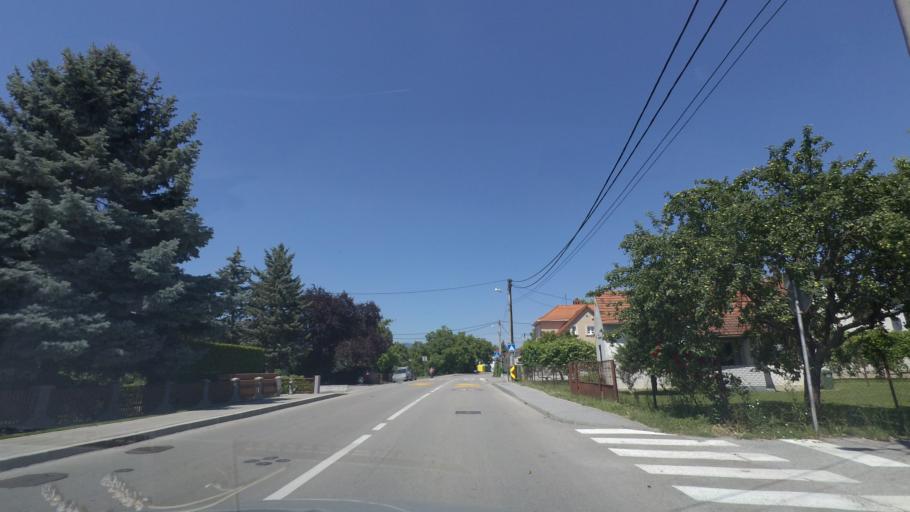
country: HR
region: Grad Zagreb
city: Zadvorsko
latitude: 45.7620
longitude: 15.9156
